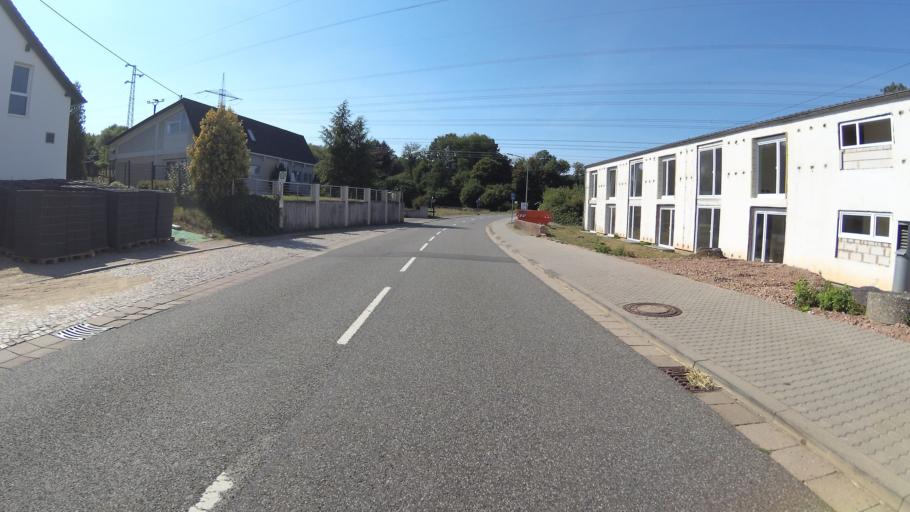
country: DE
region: Saarland
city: Eppelborn
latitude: 49.3783
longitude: 6.9667
